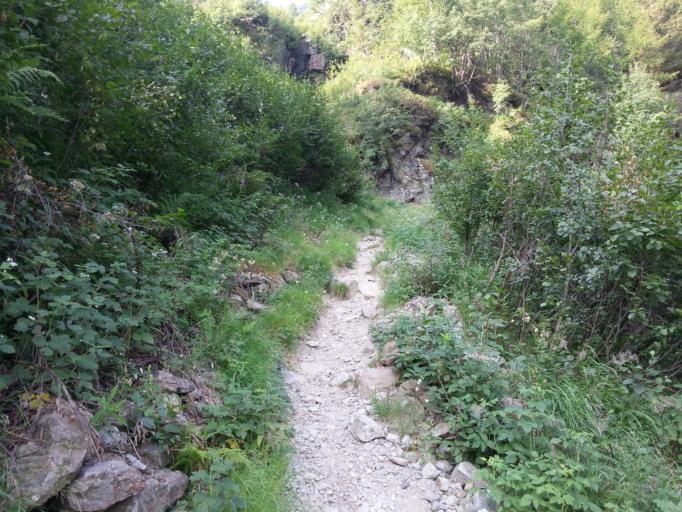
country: IT
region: Lombardy
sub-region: Provincia di Sondrio
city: Gerola Alta
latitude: 46.0583
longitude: 9.5289
